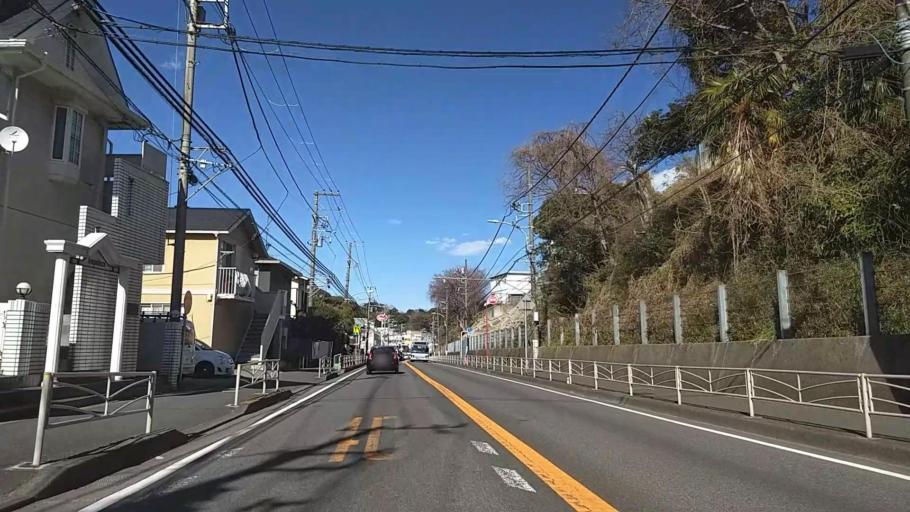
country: JP
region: Kanagawa
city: Yokohama
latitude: 35.3648
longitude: 139.6310
